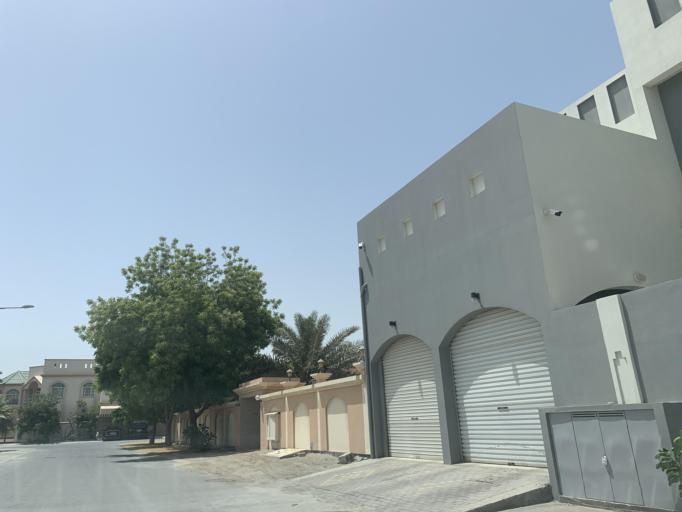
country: BH
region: Northern
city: Ar Rifa'
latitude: 26.1556
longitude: 50.5810
